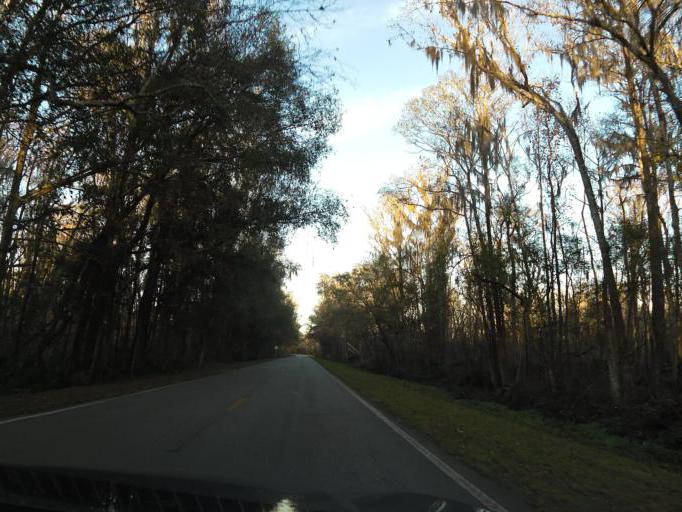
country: US
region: Florida
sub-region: Clay County
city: Green Cove Springs
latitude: 29.8608
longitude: -81.5493
